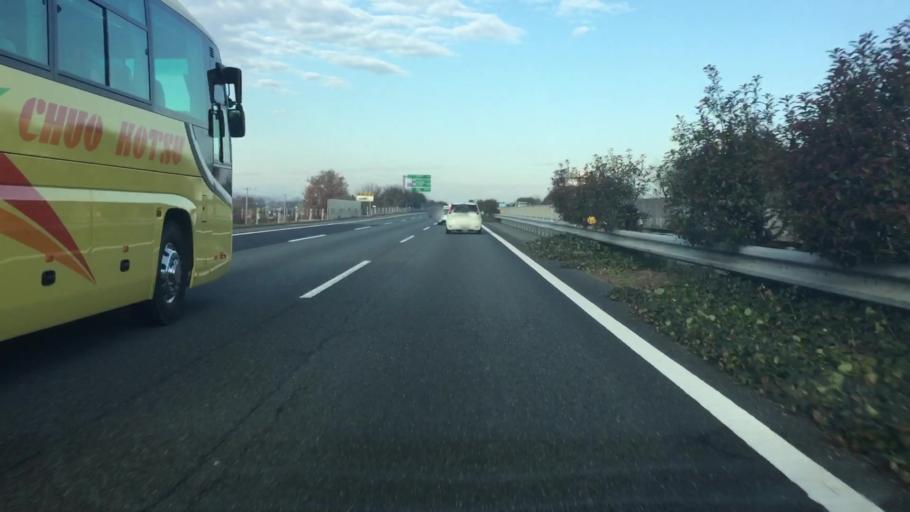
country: JP
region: Saitama
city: Yorii
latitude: 36.1301
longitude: 139.2383
